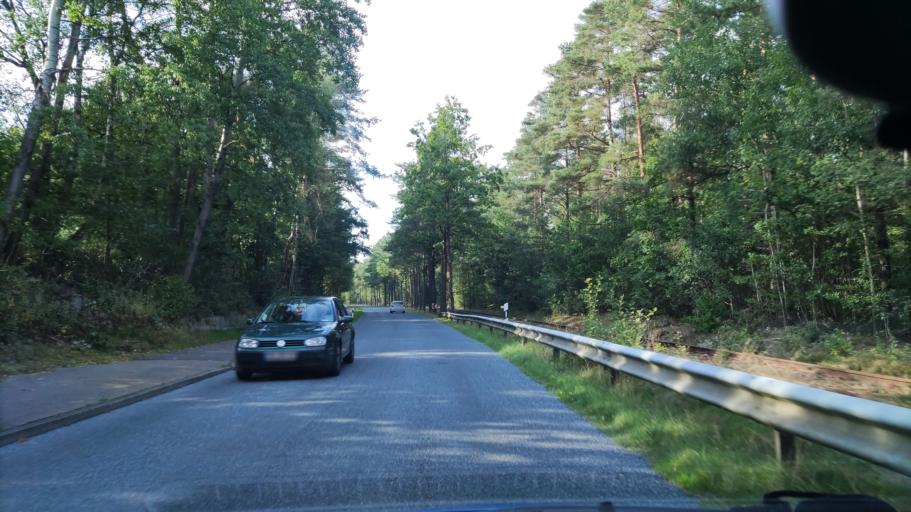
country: DE
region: Lower Saxony
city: Munster
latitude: 52.9857
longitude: 10.1265
